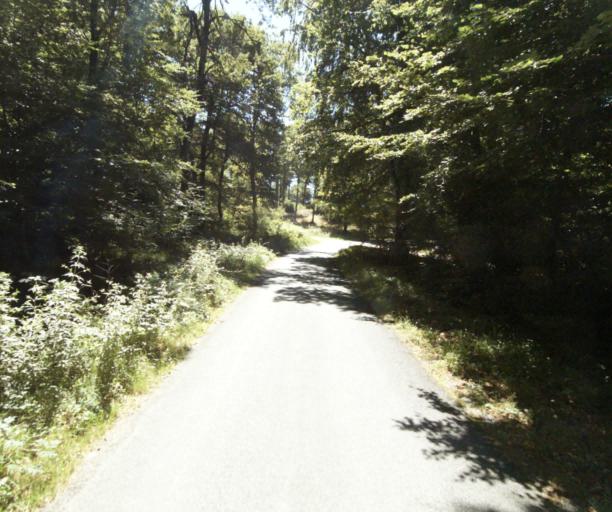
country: FR
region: Midi-Pyrenees
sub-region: Departement du Tarn
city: Dourgne
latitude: 43.4168
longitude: 2.1875
